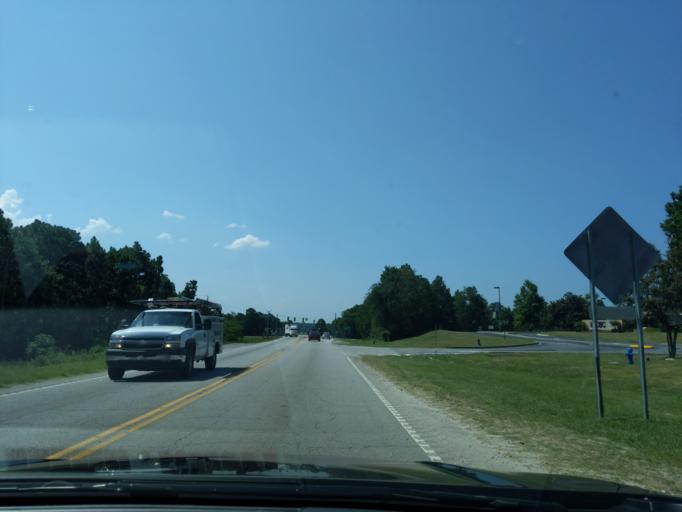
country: US
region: South Carolina
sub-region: Lexington County
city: Red Bank
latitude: 33.9304
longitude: -81.2907
